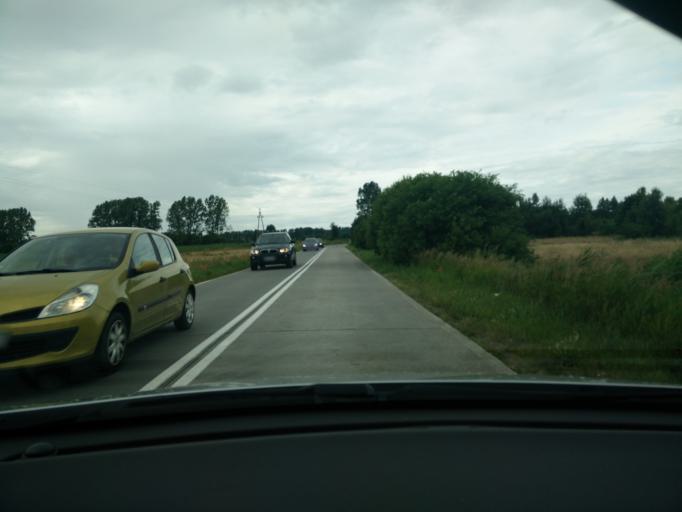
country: PL
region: Pomeranian Voivodeship
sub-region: Powiat pucki
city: Mrzezino
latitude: 54.6252
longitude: 18.4377
